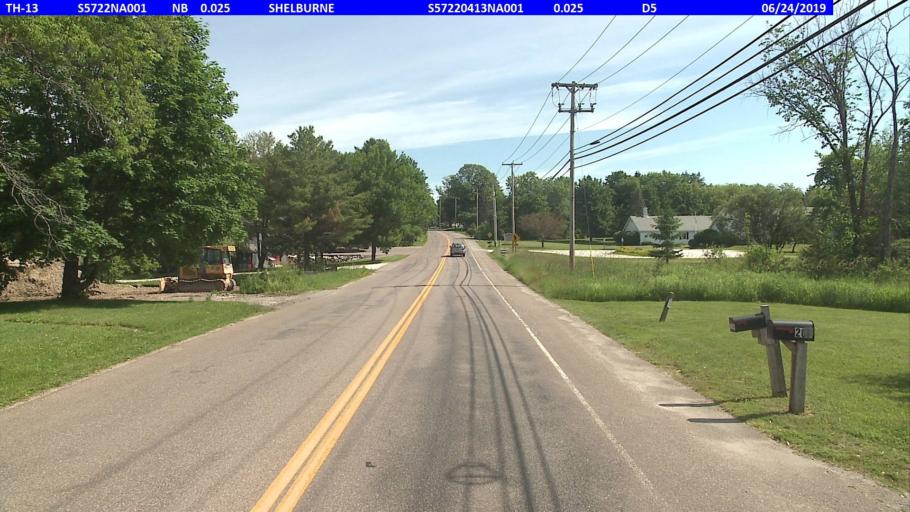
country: US
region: Vermont
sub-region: Chittenden County
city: Burlington
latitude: 44.3883
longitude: -73.2226
